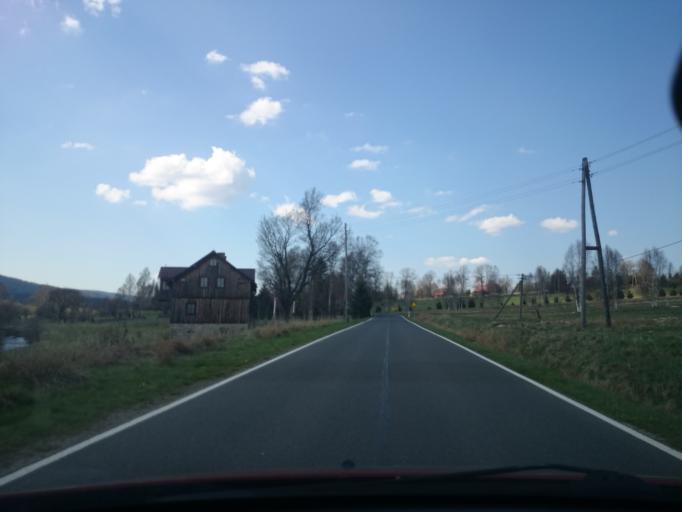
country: PL
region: Lower Silesian Voivodeship
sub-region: Powiat klodzki
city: Szczytna
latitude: 50.3026
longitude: 16.4547
